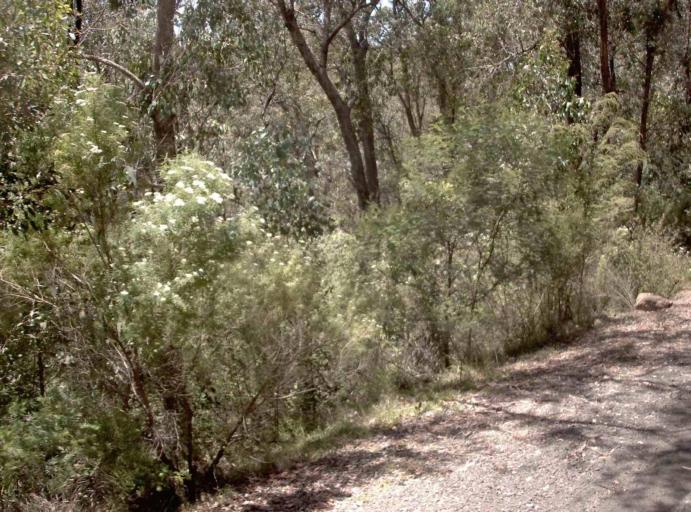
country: AU
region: Victoria
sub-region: East Gippsland
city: Lakes Entrance
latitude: -37.6200
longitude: 147.8815
